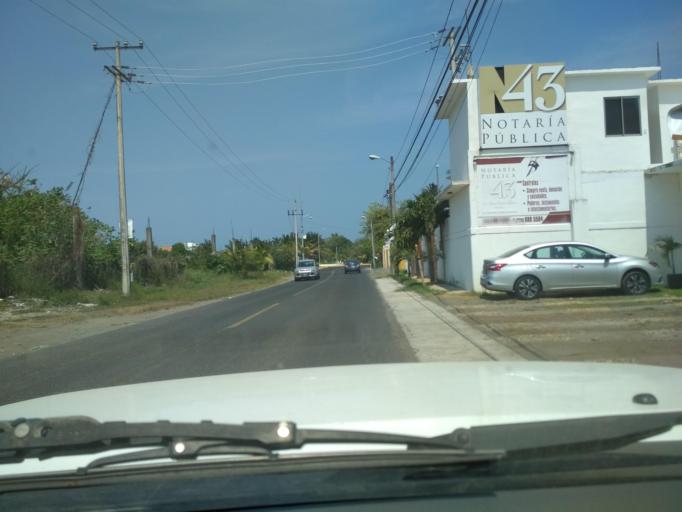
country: MX
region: Veracruz
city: Boca del Rio
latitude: 19.0960
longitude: -96.1167
